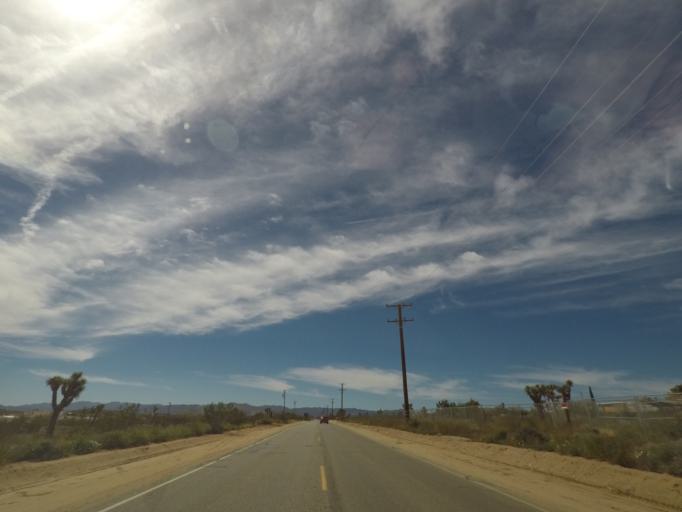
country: US
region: California
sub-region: San Bernardino County
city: Joshua Tree
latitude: 34.1880
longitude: -116.3695
